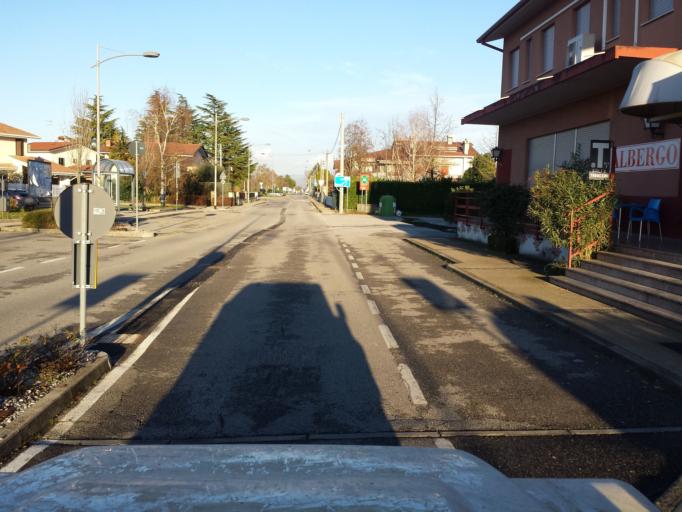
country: IT
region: Friuli Venezia Giulia
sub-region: Provincia di Gorizia
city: Villesse
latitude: 45.8678
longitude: 13.4467
